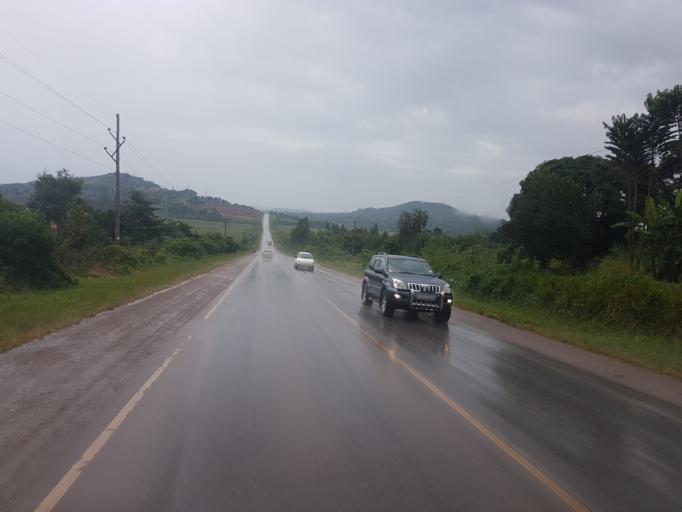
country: UG
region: Central Region
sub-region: Mpigi District
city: Mpigi
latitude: 0.1888
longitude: 32.2921
